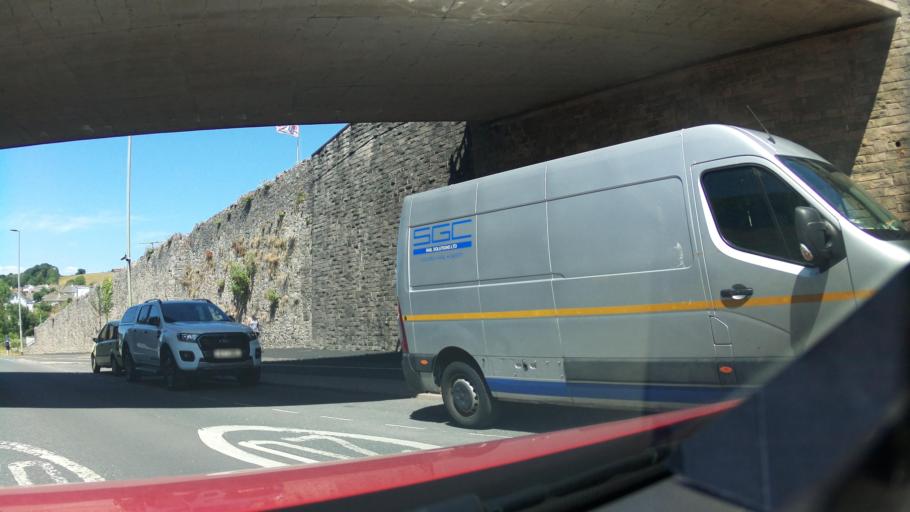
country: GB
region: England
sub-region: Devon
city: Kingskerswell
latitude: 50.4980
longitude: -3.5784
